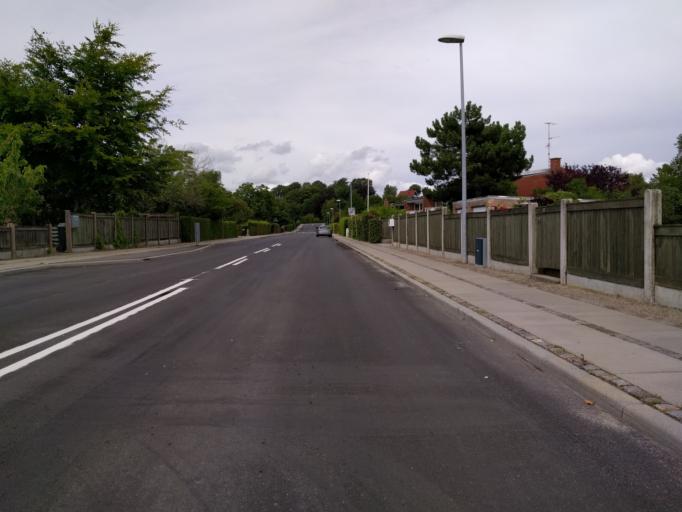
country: DK
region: Central Jutland
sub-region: Skanderborg Kommune
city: Ry
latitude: 56.0885
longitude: 9.7652
